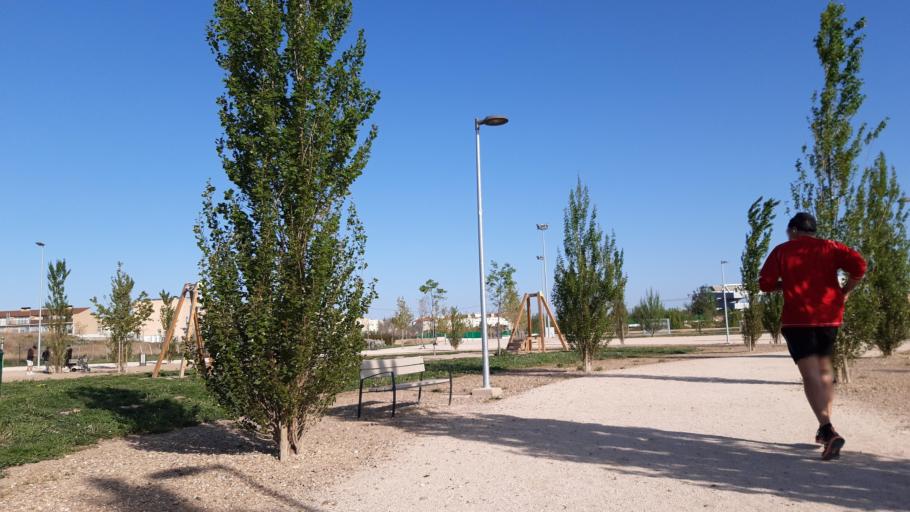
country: ES
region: Aragon
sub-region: Provincia de Zaragoza
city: Utebo
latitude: 41.7051
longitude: -0.9908
